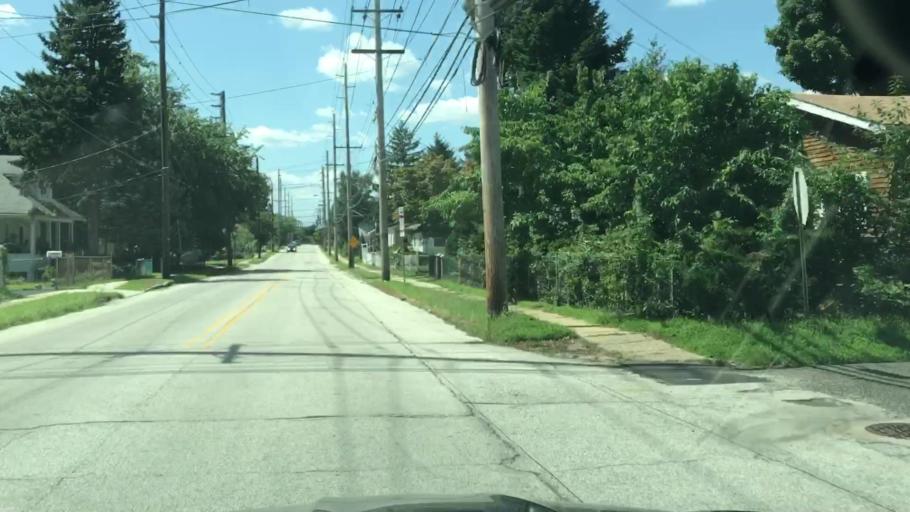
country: US
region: New Jersey
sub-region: Camden County
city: Pennsauken
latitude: 39.9807
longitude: -75.0466
